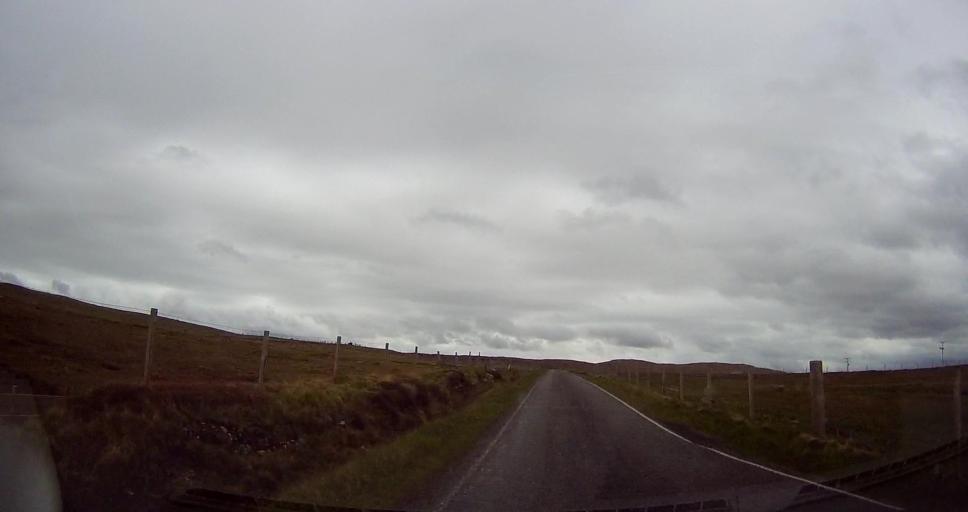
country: GB
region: Scotland
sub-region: Shetland Islands
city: Lerwick
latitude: 60.4861
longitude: -1.4844
